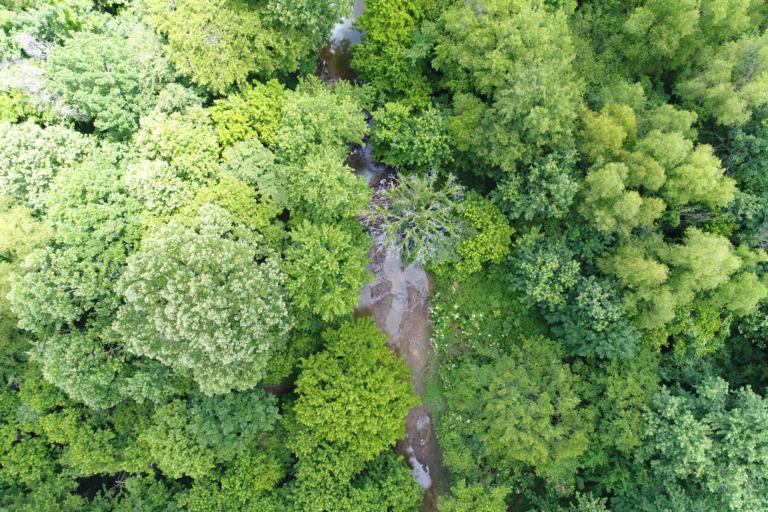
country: US
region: Mississippi
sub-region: De Soto County
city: Walls
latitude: 34.9180
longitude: -90.1992
